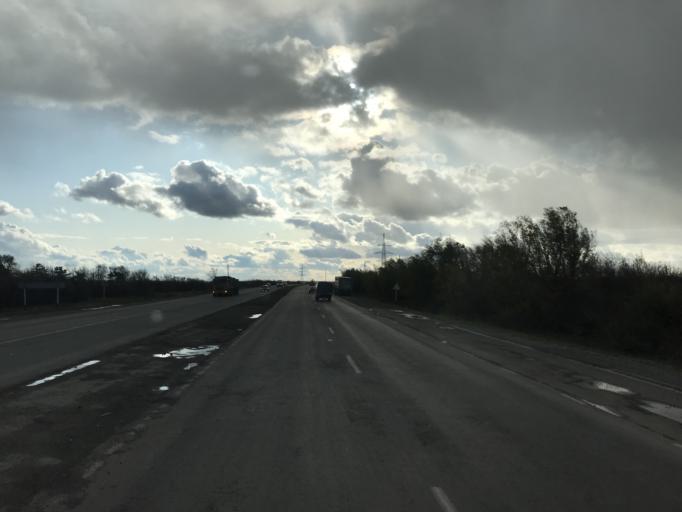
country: KZ
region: Qostanay
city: Kostanay
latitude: 53.1231
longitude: 63.5497
